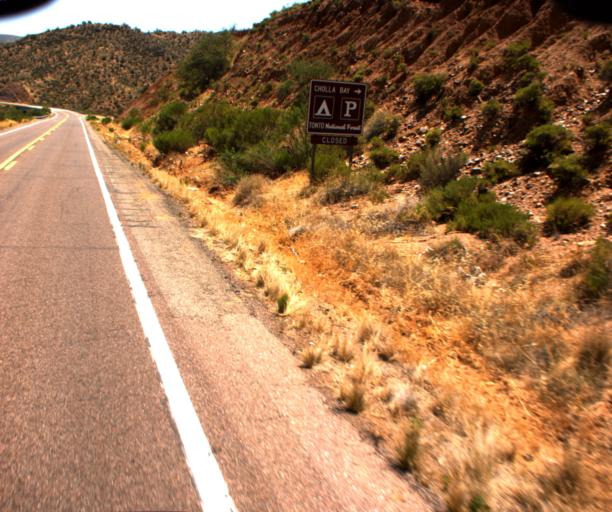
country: US
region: Arizona
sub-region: Gila County
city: Tonto Basin
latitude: 33.7211
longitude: -111.2050
